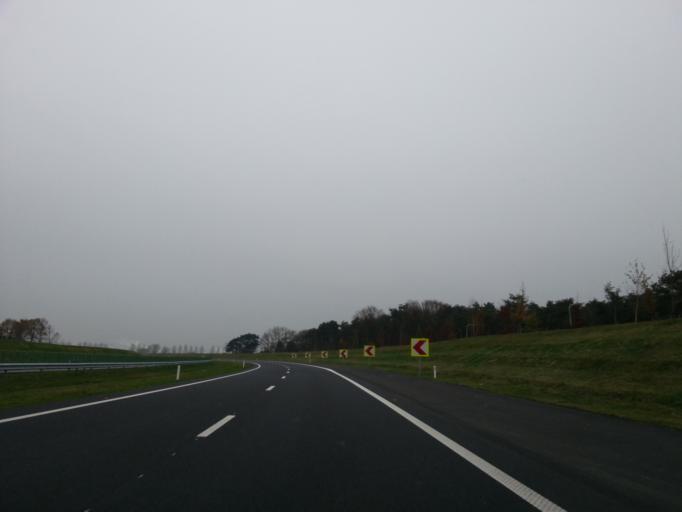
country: NL
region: North Brabant
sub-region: Gemeente Bergen op Zoom
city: Lepelstraat
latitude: 51.5516
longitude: 4.2965
